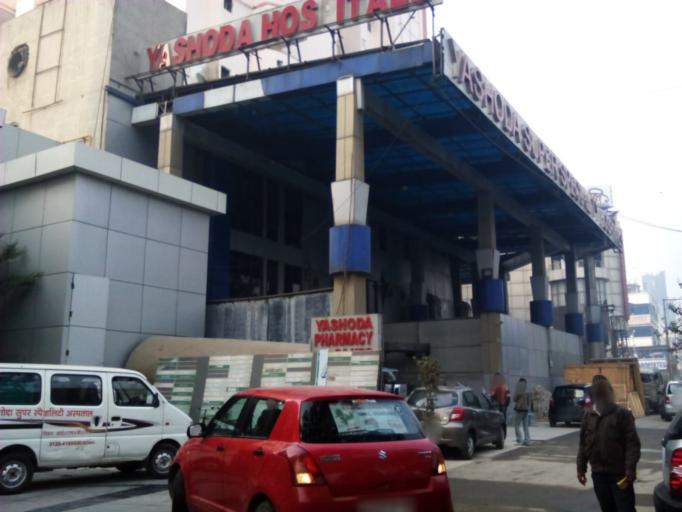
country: IN
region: Uttar Pradesh
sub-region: Gautam Buddha Nagar
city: Noida
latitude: 28.6454
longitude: 77.3287
